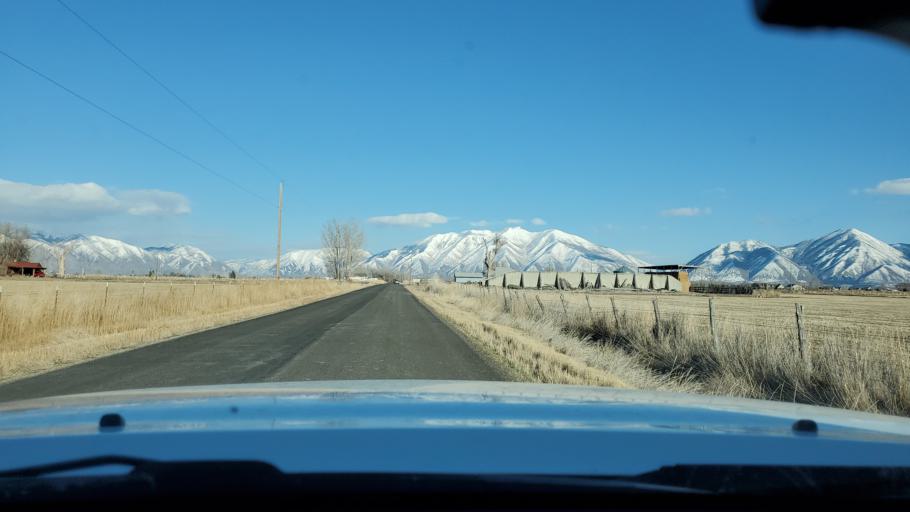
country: US
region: Utah
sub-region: Utah County
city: Benjamin
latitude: 40.1143
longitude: -111.7624
